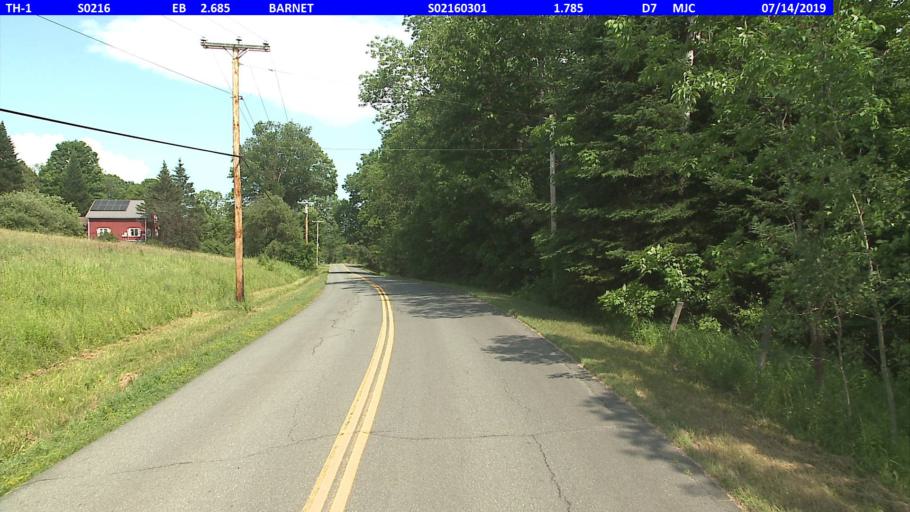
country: US
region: Vermont
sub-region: Caledonia County
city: Saint Johnsbury
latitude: 44.3106
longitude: -72.1189
